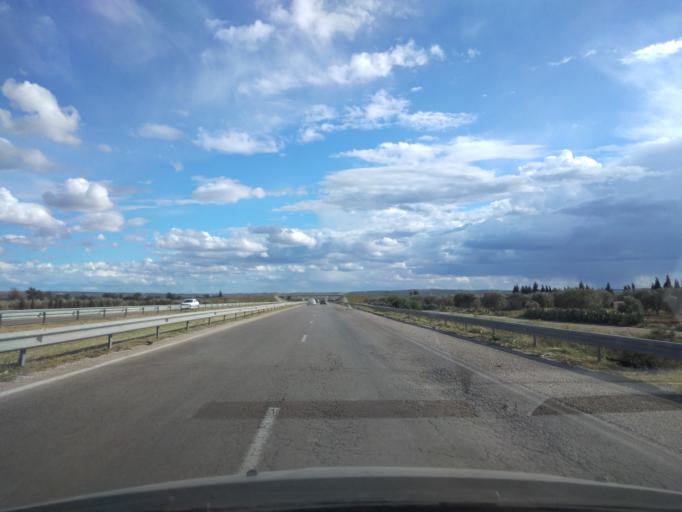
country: TN
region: Al Munastir
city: Manzil Kamil
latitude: 35.5954
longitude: 10.6028
